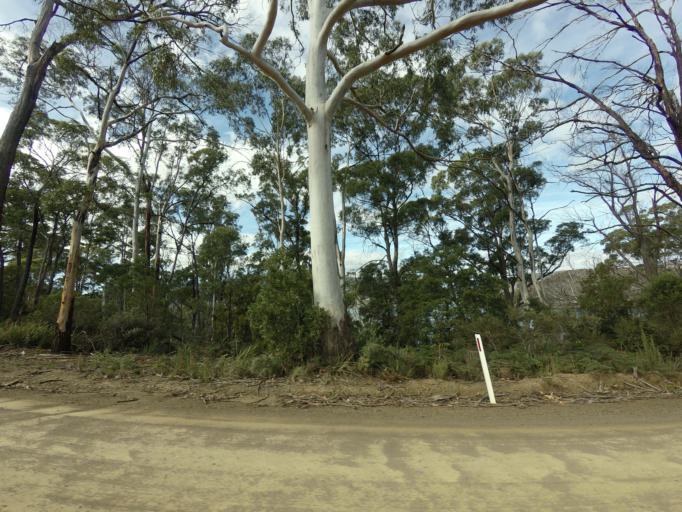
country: AU
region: Tasmania
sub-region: Clarence
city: Sandford
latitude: -43.0949
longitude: 147.7221
